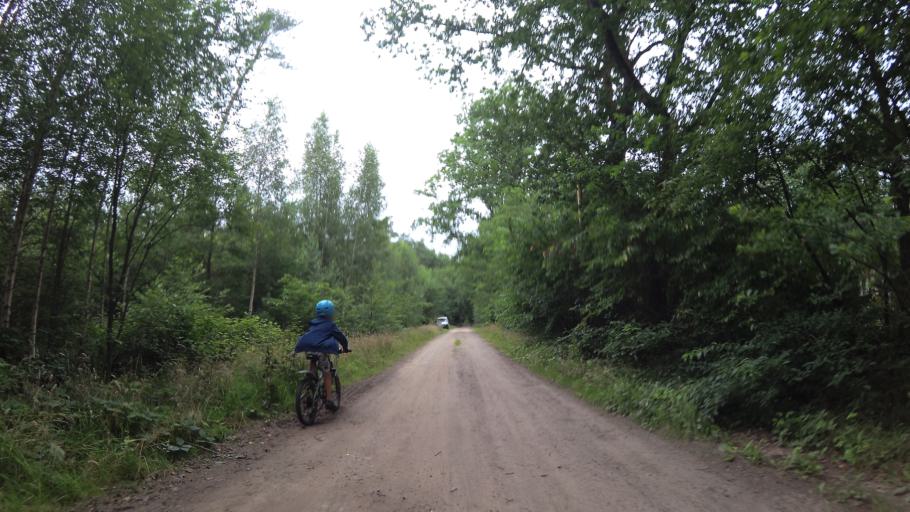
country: DE
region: Lower Saxony
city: Fresenburg
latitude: 52.8771
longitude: 7.2991
